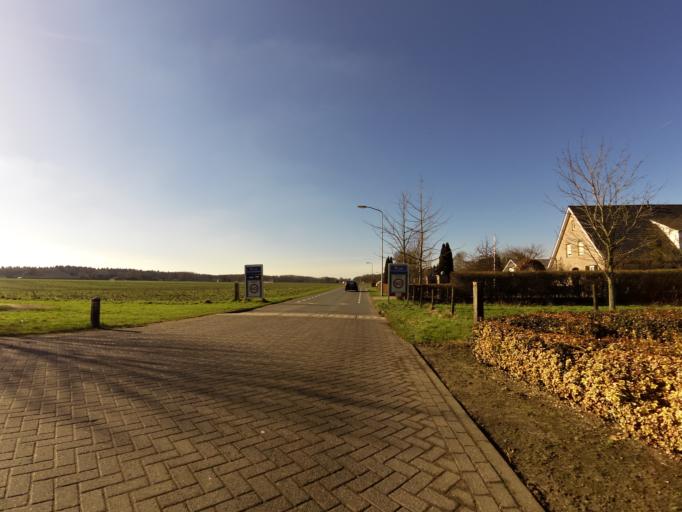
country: NL
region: Gelderland
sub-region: Gemeente Doesburg
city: Doesburg
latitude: 51.9631
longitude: 6.2000
